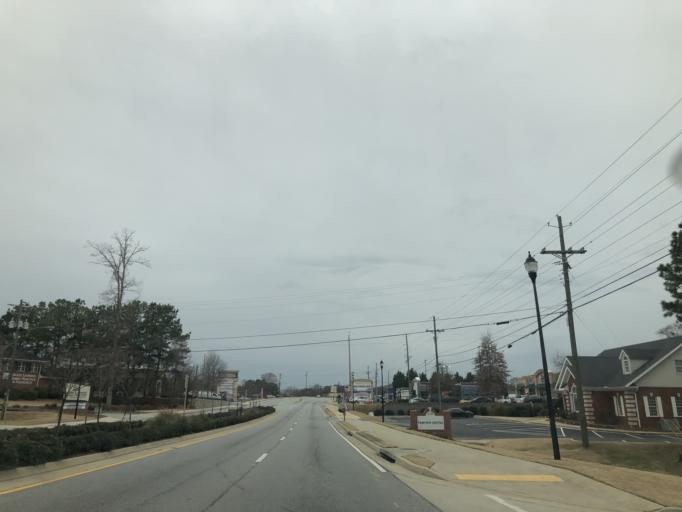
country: US
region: Georgia
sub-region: Henry County
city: Stockbridge
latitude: 33.6197
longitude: -84.2418
